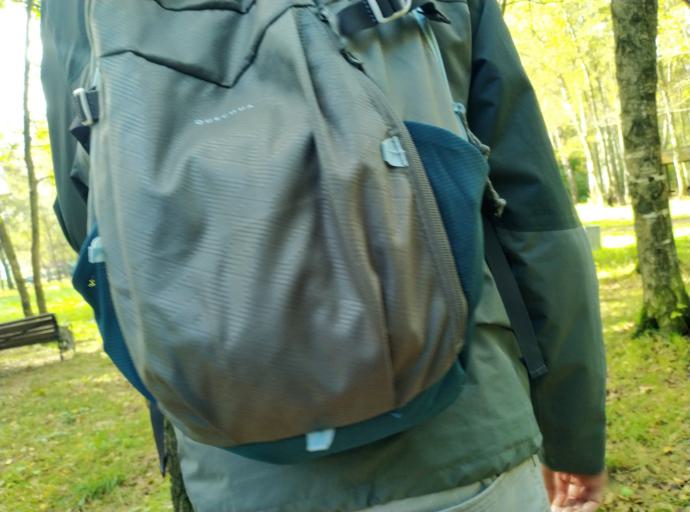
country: RU
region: Moscow
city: Khimki
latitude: 55.8681
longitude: 37.4255
